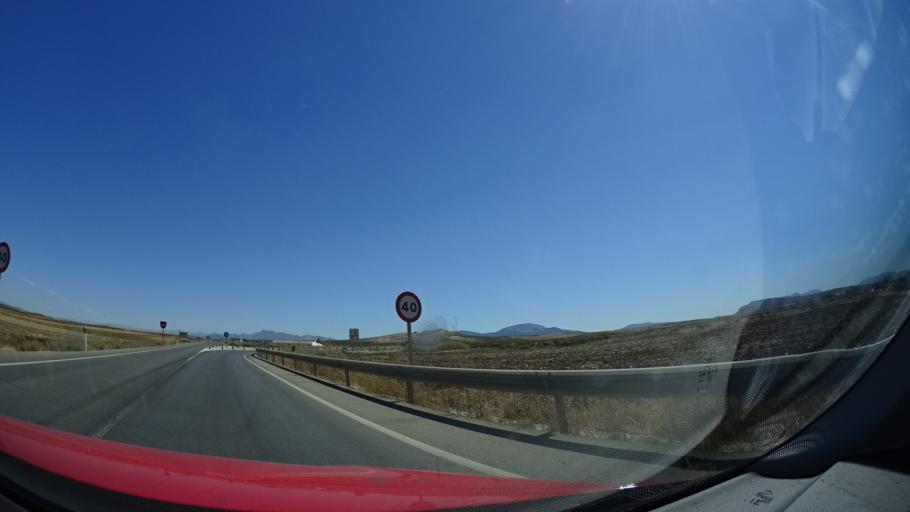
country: ES
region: Andalusia
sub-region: Provincia de Malaga
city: Campillos
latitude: 37.0498
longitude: -4.8472
